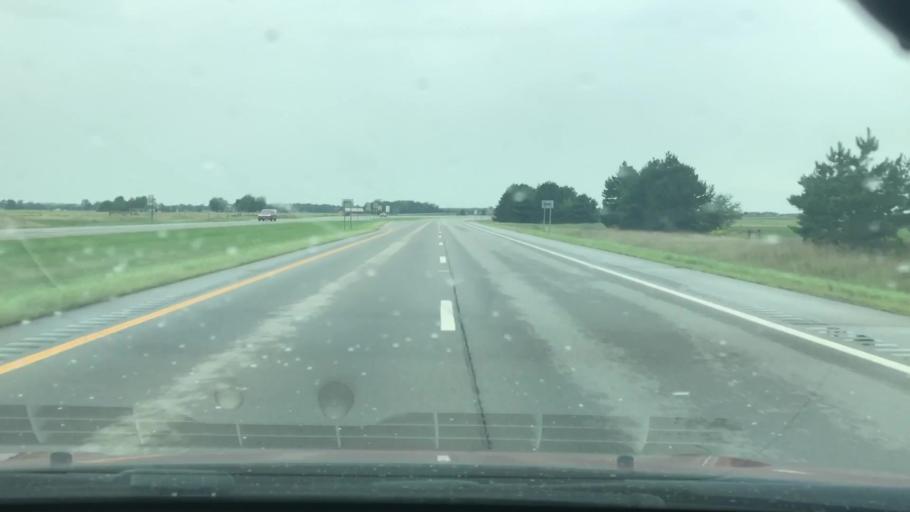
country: US
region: Ohio
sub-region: Wyandot County
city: Carey
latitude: 40.9653
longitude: -83.4750
